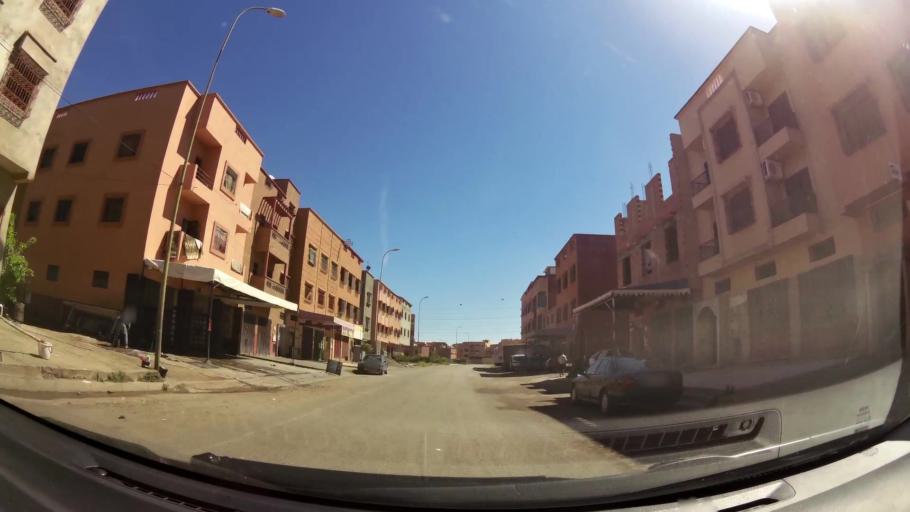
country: MA
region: Marrakech-Tensift-Al Haouz
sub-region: Marrakech
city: Marrakesh
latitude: 31.5736
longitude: -8.0627
